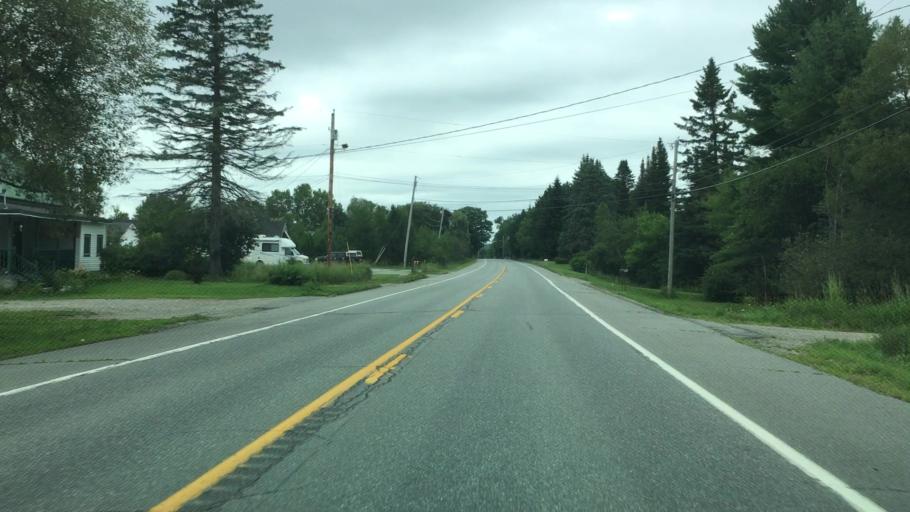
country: US
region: Maine
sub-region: Waldo County
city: Winterport
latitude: 44.6830
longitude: -68.8446
